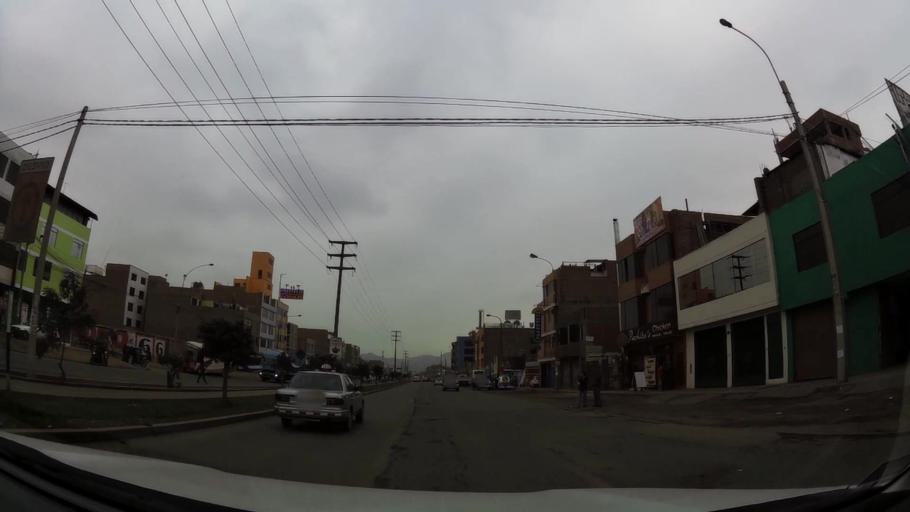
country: PE
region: Lima
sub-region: Lima
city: Vitarte
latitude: -12.0370
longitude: -76.9522
